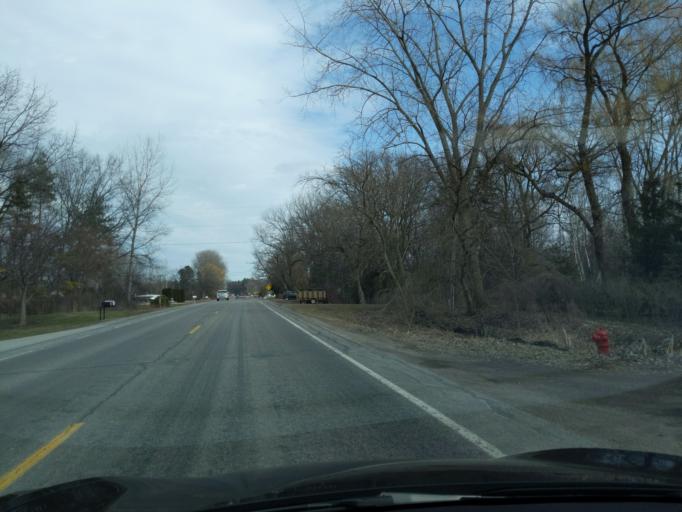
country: US
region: Michigan
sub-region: Bay County
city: Bay City
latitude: 43.6672
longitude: -83.9192
